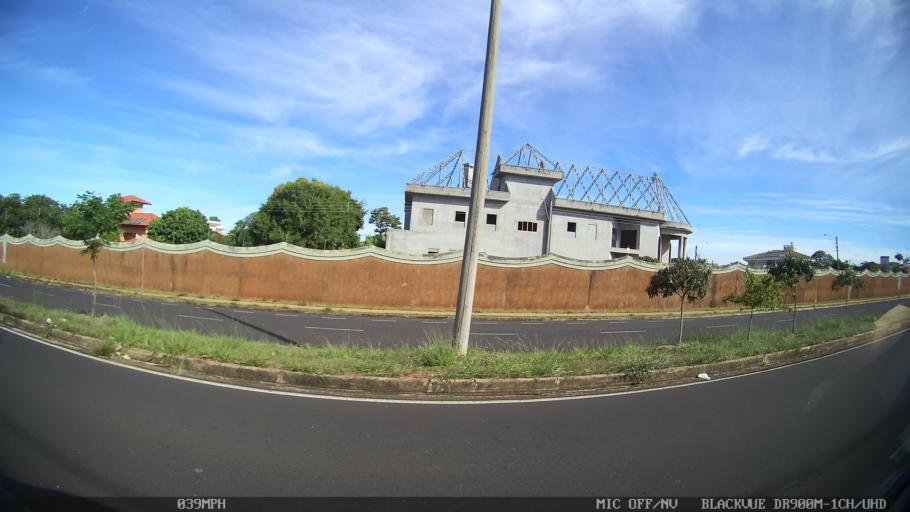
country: BR
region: Sao Paulo
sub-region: Sao Jose Do Rio Preto
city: Sao Jose do Rio Preto
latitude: -20.8084
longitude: -49.3459
